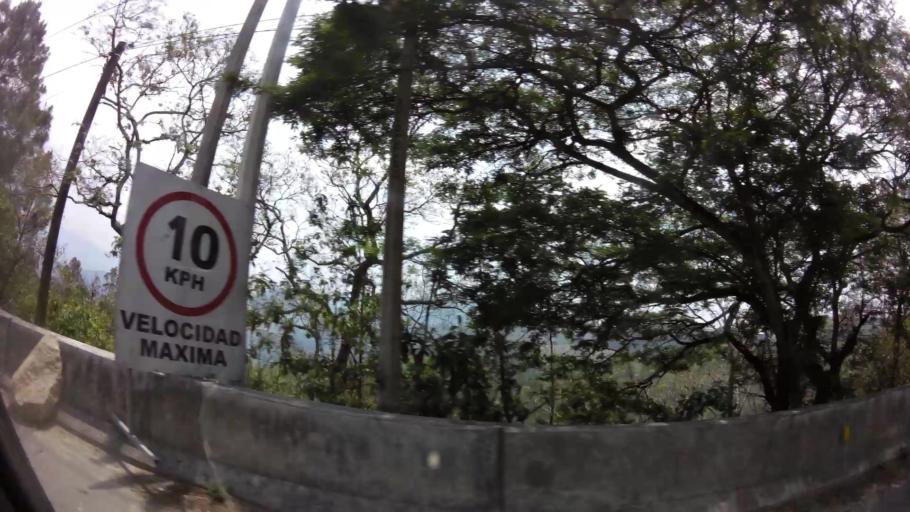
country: HN
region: Comayagua
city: El Socorro
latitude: 14.6512
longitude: -87.9338
